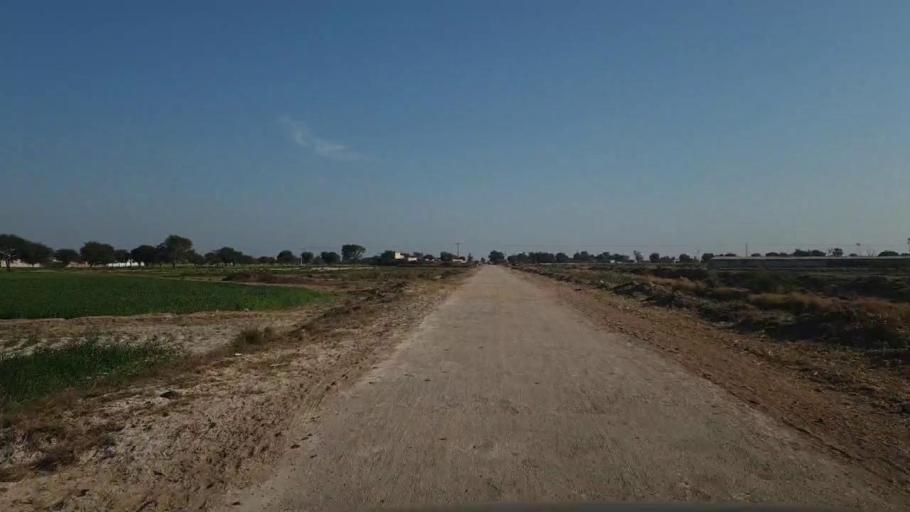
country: PK
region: Sindh
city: Shahpur Chakar
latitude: 26.1688
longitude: 68.6598
